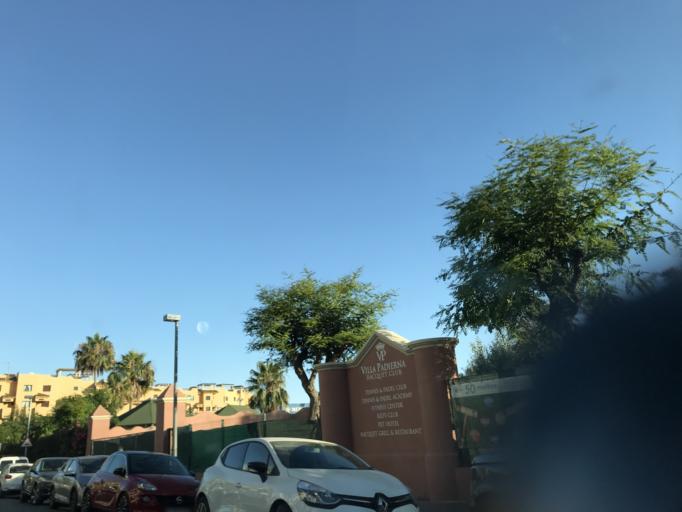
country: ES
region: Andalusia
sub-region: Provincia de Malaga
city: Benahavis
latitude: 36.4594
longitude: -5.0475
